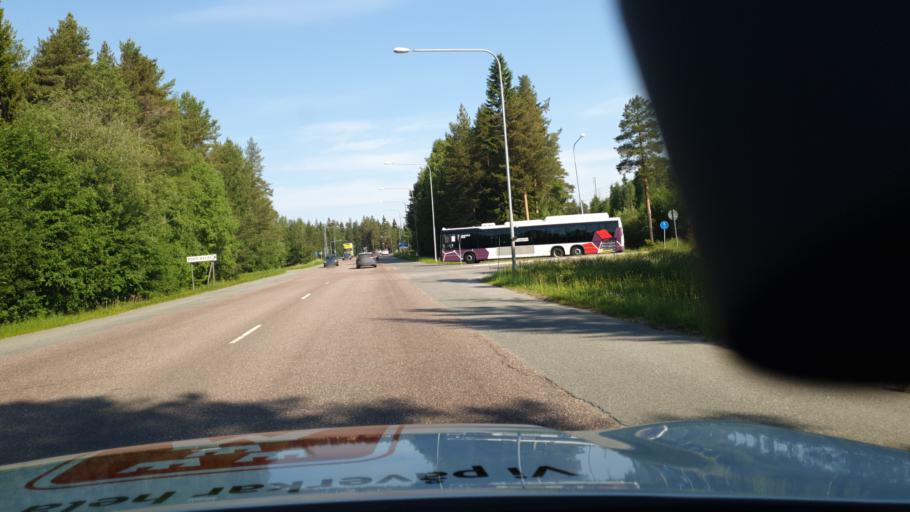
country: SE
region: Vaesterbotten
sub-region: Skelleftea Kommun
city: Skelleftea
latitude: 64.7598
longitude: 21.0068
